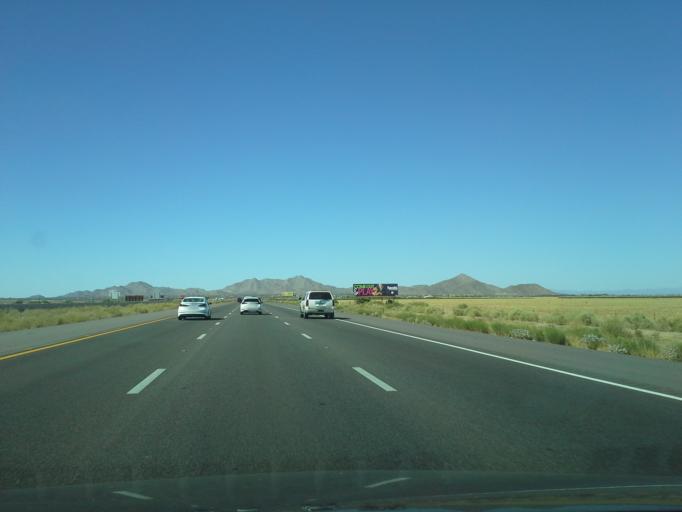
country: US
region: Arizona
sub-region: Pinal County
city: Casa Grande
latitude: 32.8961
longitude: -111.6867
